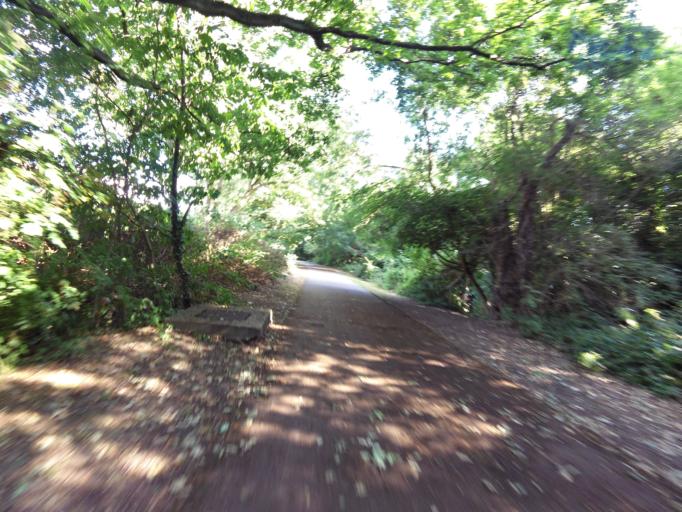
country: GB
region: England
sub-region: Greater London
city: Wood Green
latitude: 51.6255
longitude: -0.1415
